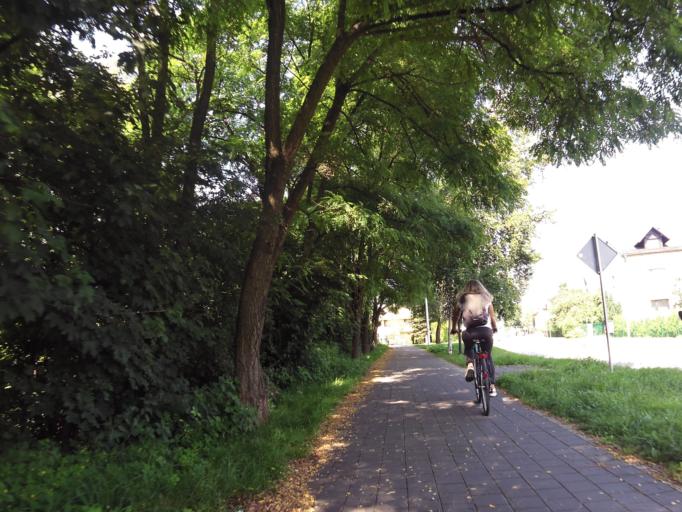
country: PL
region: Silesian Voivodeship
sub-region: Powiat zywiecki
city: Wegierska Gorka
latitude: 49.6119
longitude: 19.1264
